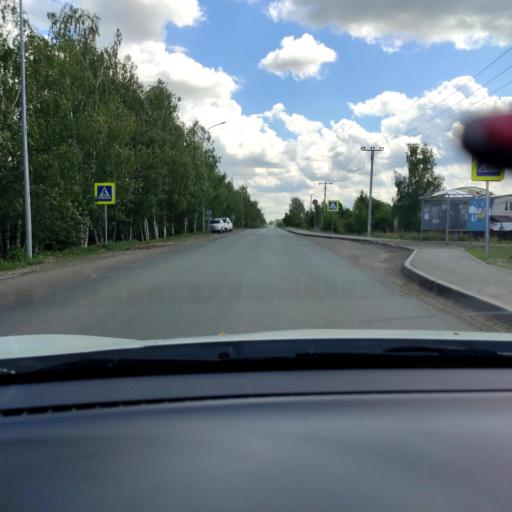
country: RU
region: Tatarstan
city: Stolbishchi
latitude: 55.6996
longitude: 49.1826
